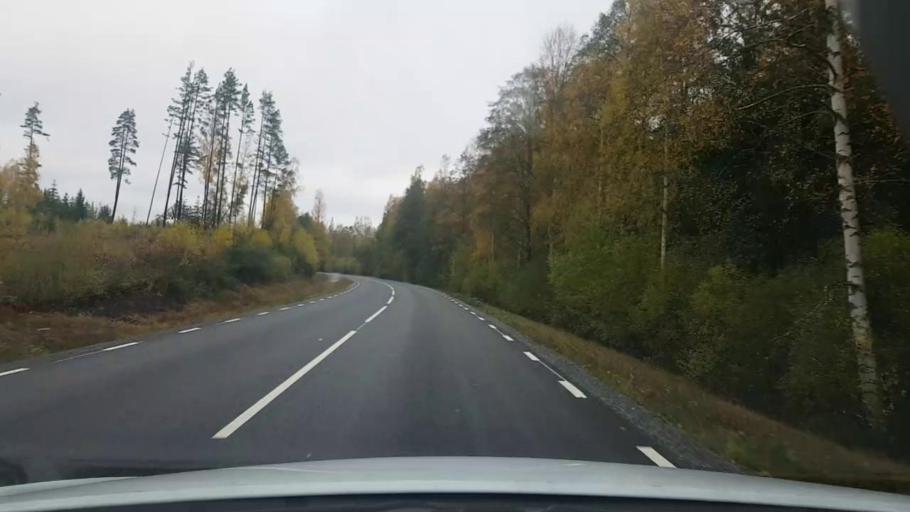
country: SE
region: OErebro
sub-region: Laxa Kommun
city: Laxa
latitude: 58.8163
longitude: 14.5508
